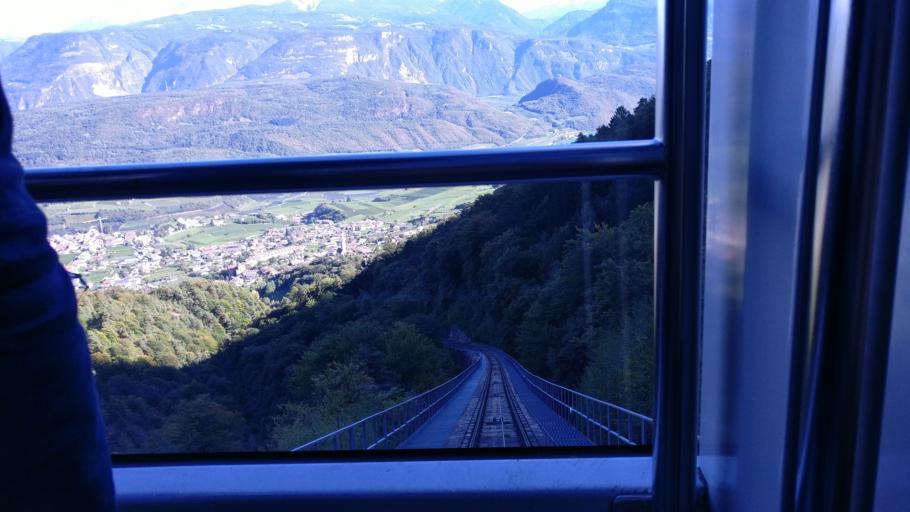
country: IT
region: Trentino-Alto Adige
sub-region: Bolzano
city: Caldaro sulla Strada del Vino
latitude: 46.4132
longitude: 11.2192
